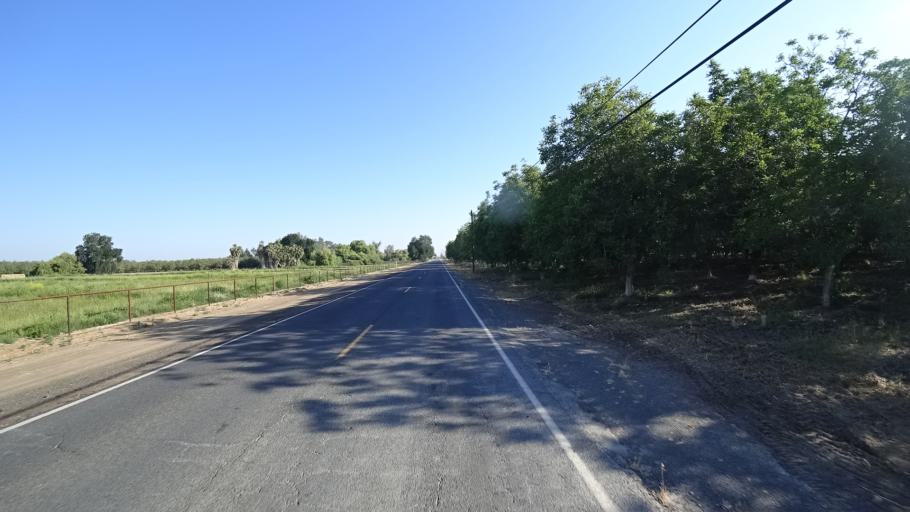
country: US
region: California
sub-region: Kings County
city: Armona
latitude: 36.2806
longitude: -119.7091
